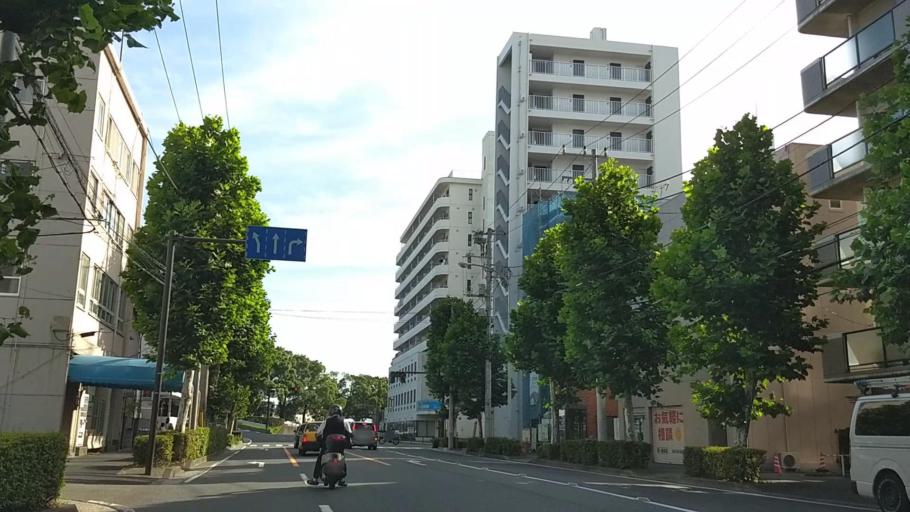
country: JP
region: Kanagawa
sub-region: Kawasaki-shi
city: Kawasaki
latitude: 35.5077
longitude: 139.6843
